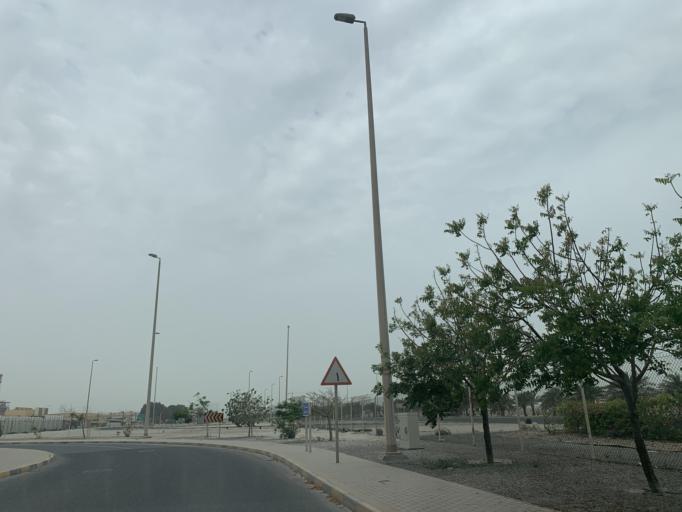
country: BH
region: Muharraq
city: Al Hadd
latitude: 26.2247
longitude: 50.6678
